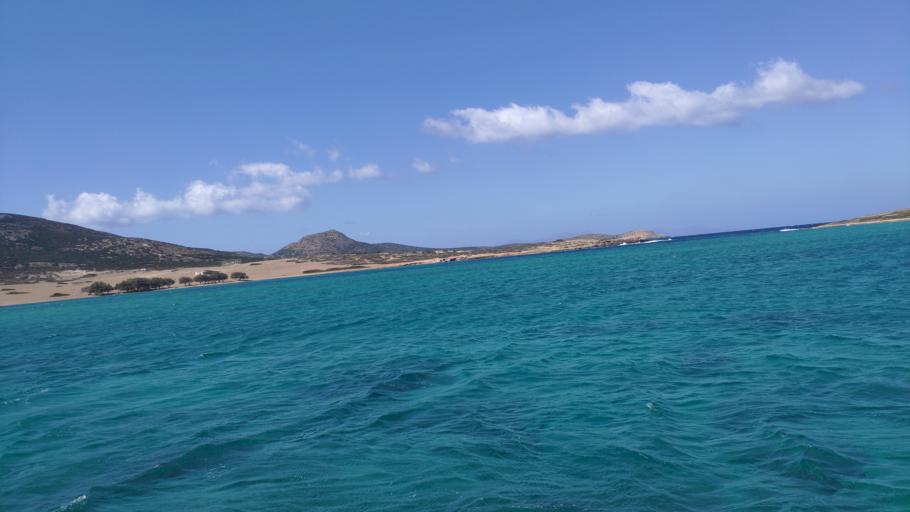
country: GR
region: South Aegean
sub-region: Nomos Kykladon
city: Antiparos
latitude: 36.9734
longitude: 25.0212
